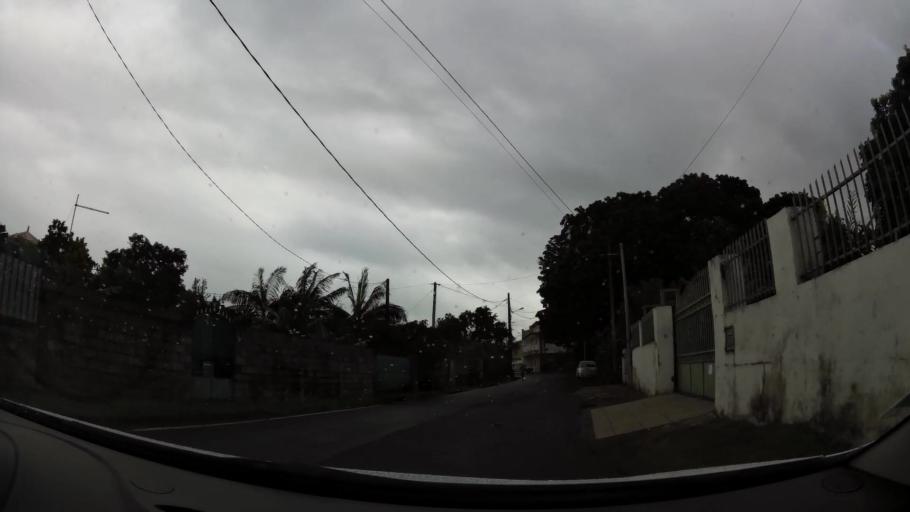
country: RE
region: Reunion
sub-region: Reunion
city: Saint-Andre
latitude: -20.9504
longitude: 55.6509
